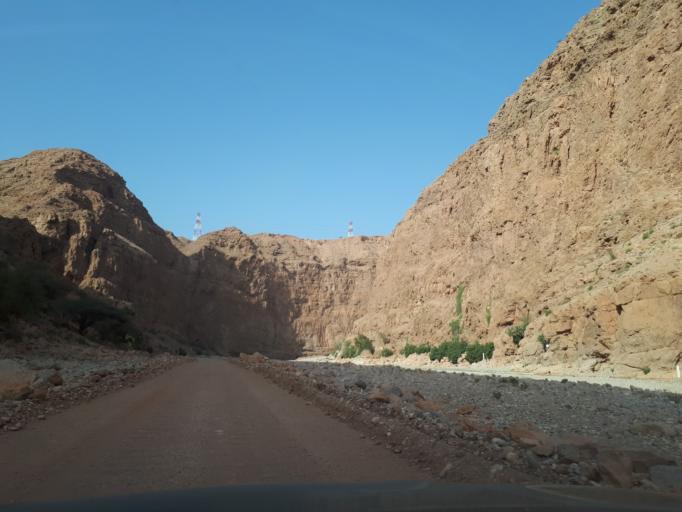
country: OM
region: Ash Sharqiyah
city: Al Qabil
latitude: 23.0767
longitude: 59.0218
